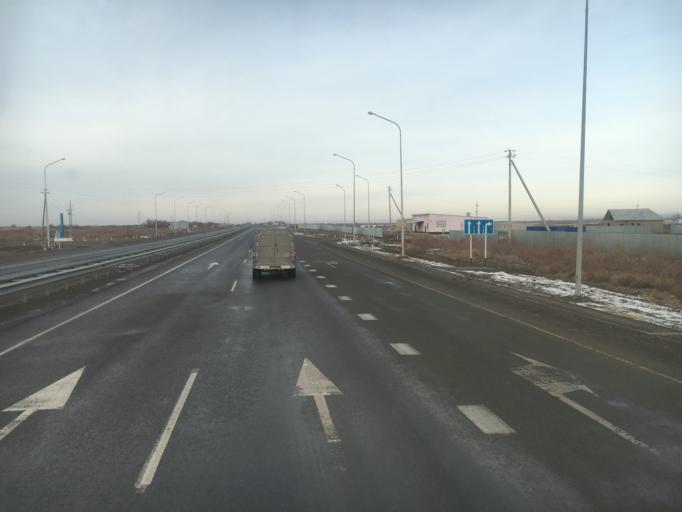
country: KZ
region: Qyzylorda
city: Shieli
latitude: 44.1395
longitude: 66.9656
